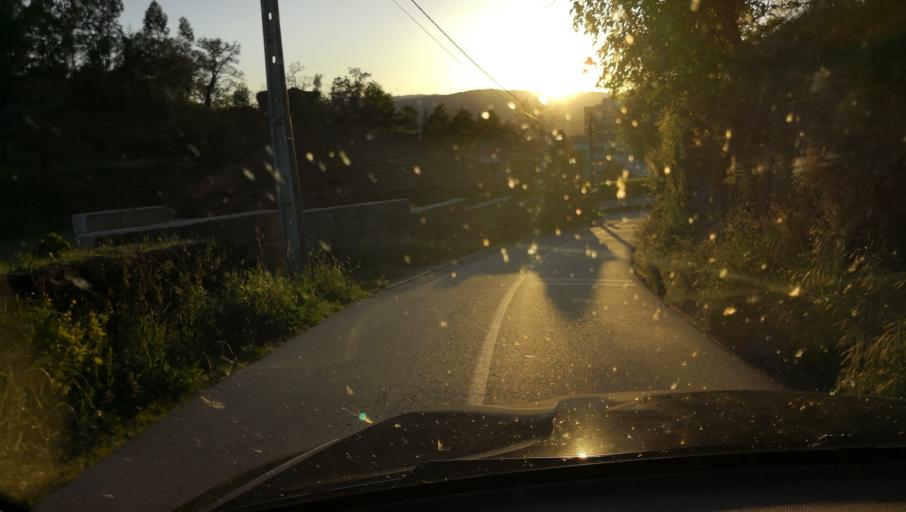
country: PT
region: Vila Real
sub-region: Mondim de Basto
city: Mondim de Basto
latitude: 41.4089
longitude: -7.9511
